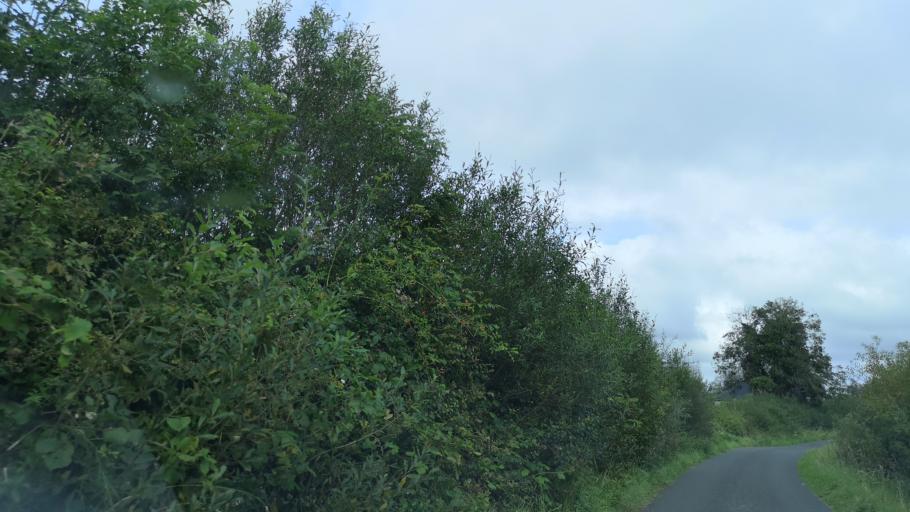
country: IE
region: Connaught
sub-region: County Galway
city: Loughrea
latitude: 53.2983
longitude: -8.6000
